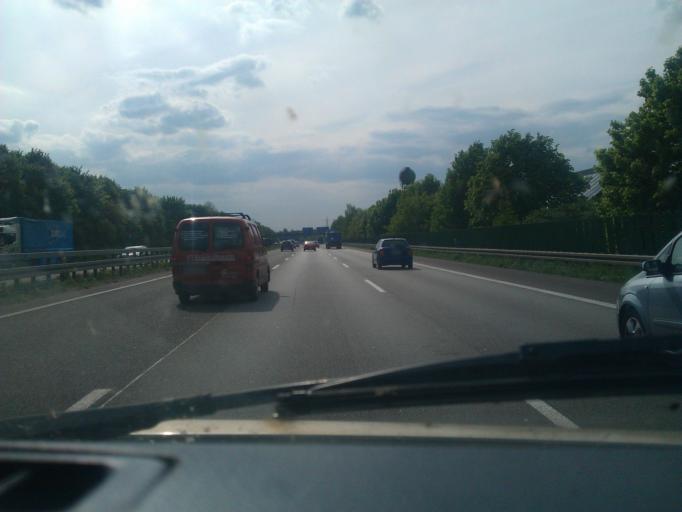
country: DE
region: North Rhine-Westphalia
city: Rheinberg
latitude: 51.4936
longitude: 6.5980
